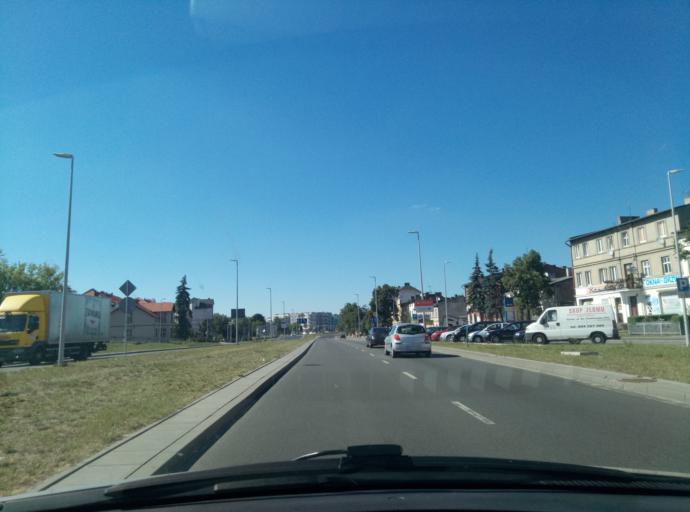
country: PL
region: Kujawsko-Pomorskie
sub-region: Torun
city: Torun
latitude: 53.0223
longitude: 18.5952
